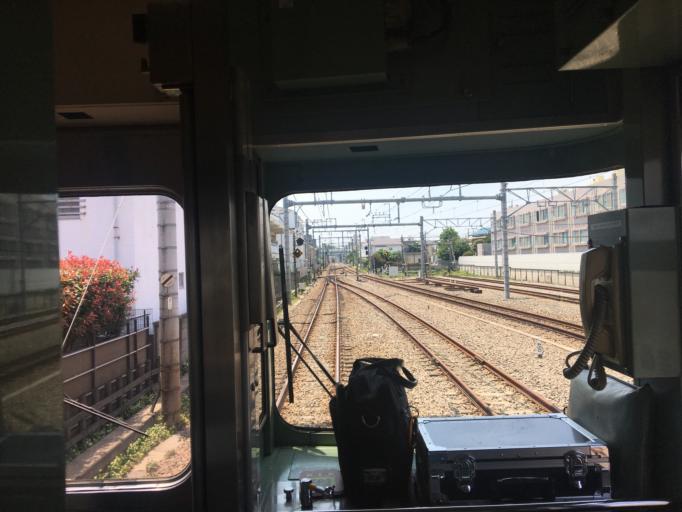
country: JP
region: Tokyo
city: Nishi-Tokyo-shi
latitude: 35.7478
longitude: 139.5627
